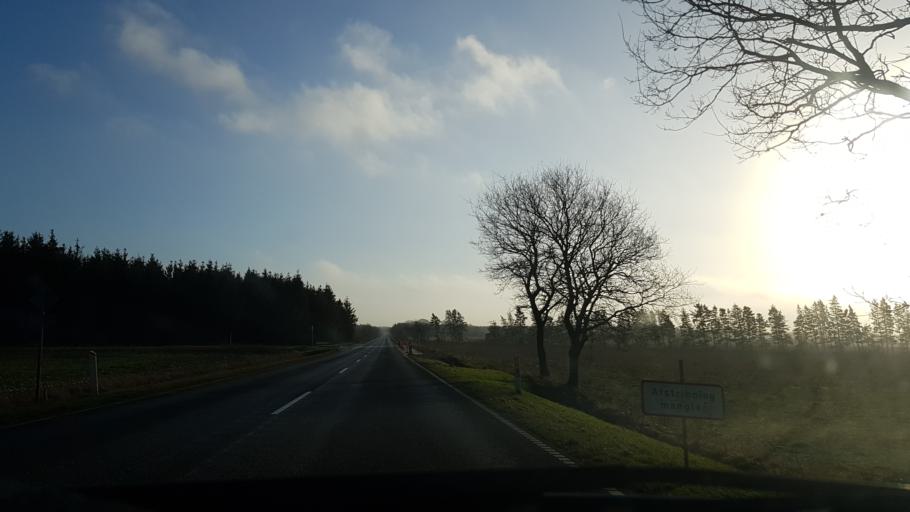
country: DK
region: South Denmark
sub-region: Tonder Kommune
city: Toftlund
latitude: 55.2126
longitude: 9.1864
